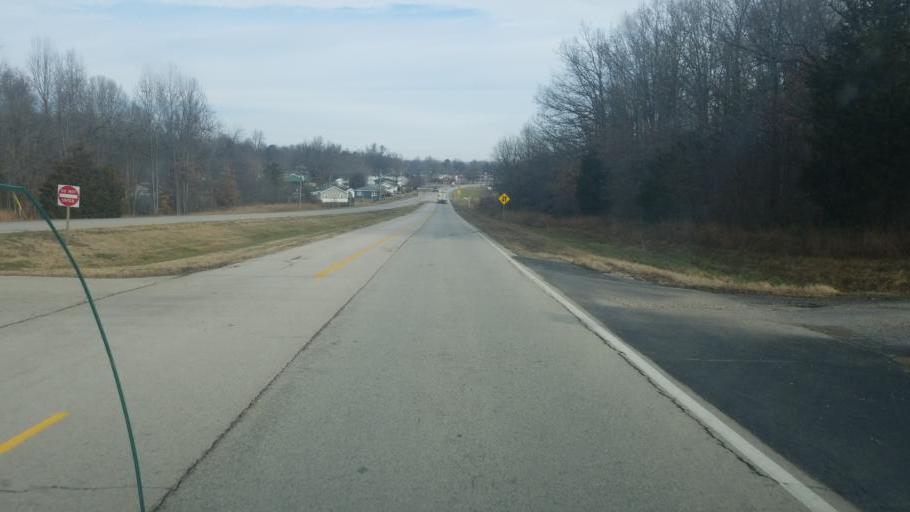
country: US
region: Missouri
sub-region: Stoddard County
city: Bloomfield
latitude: 36.8771
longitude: -89.9277
